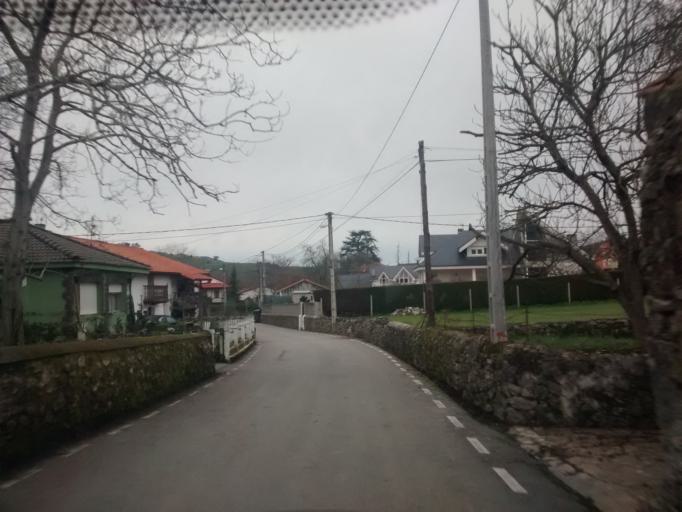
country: ES
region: Cantabria
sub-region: Provincia de Cantabria
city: Entrambasaguas
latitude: 43.3489
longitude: -3.7033
